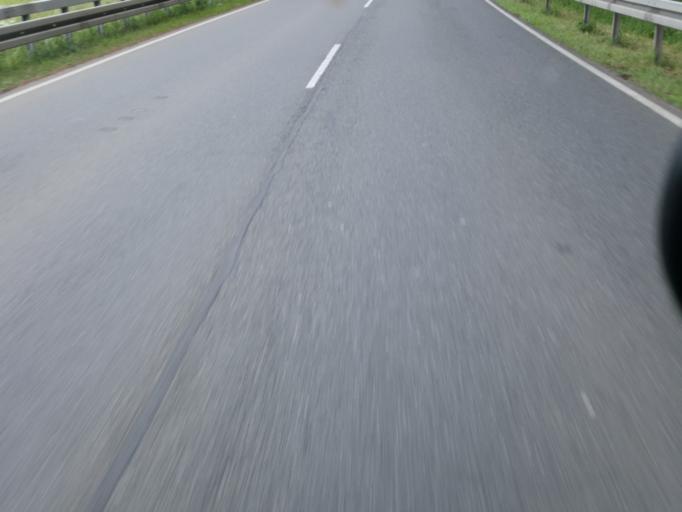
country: DE
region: Lower Saxony
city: Leese
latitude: 52.4848
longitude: 9.1330
